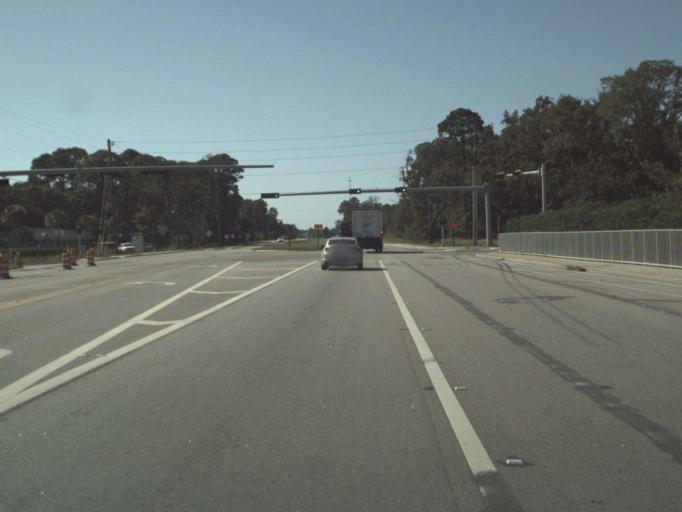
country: US
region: Florida
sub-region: Walton County
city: Seaside
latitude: 30.3885
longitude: -86.1742
